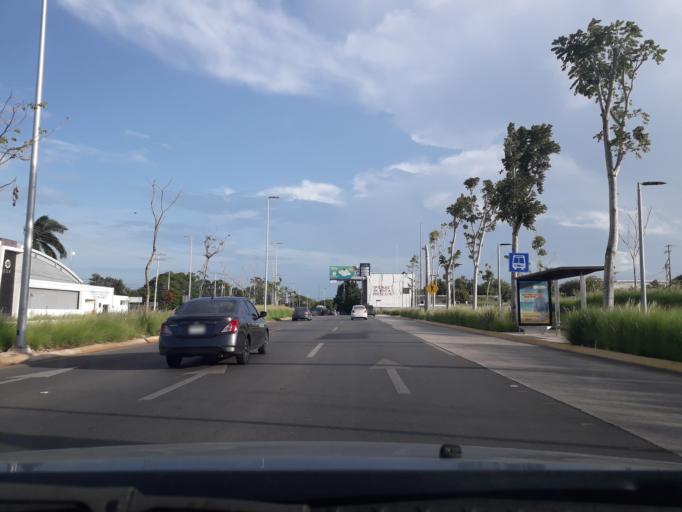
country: MX
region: Yucatan
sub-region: Merida
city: Komchen
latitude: 21.0437
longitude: -89.6295
